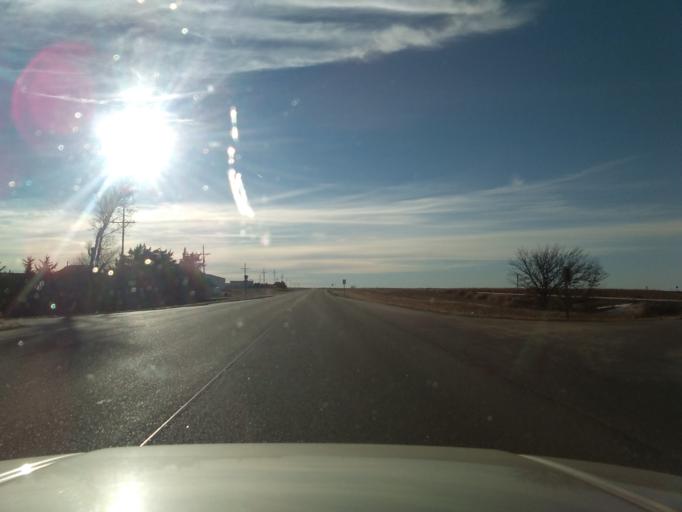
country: US
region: Kansas
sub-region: Sheridan County
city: Hoxie
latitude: 39.5385
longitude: -100.5810
